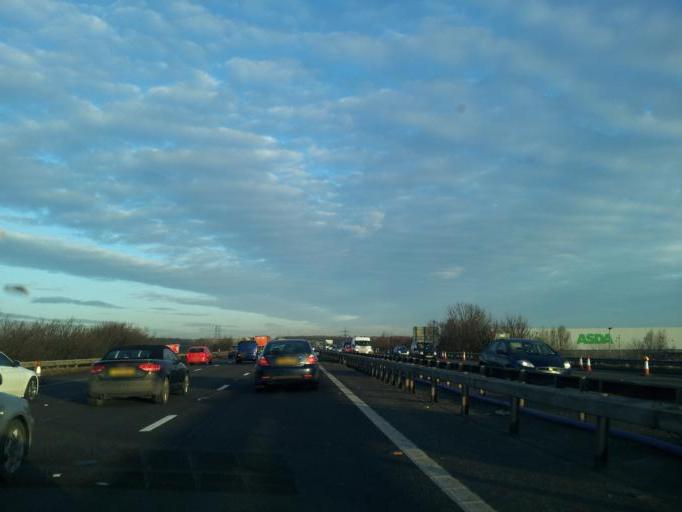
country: GB
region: England
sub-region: City and Borough of Wakefield
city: Normanton
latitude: 53.7157
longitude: -1.4211
